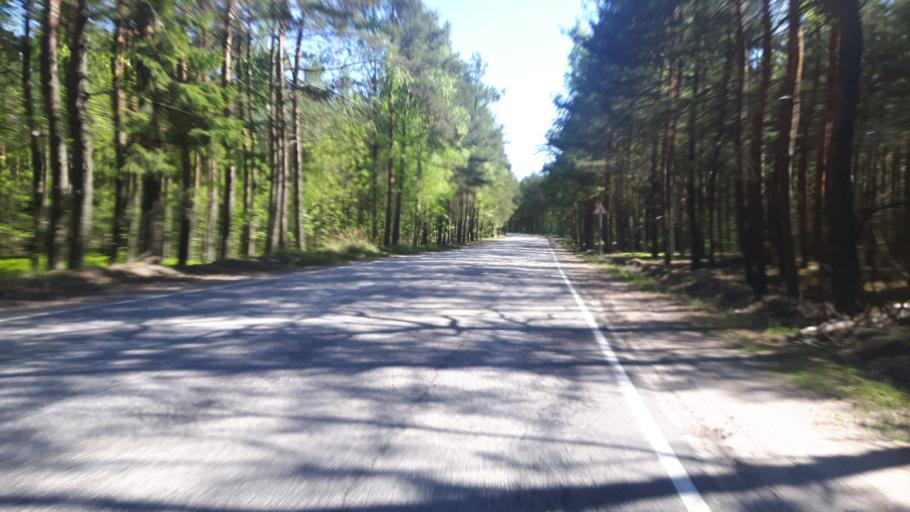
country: RU
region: Leningrad
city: Glebychevo
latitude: 60.2912
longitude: 28.8695
